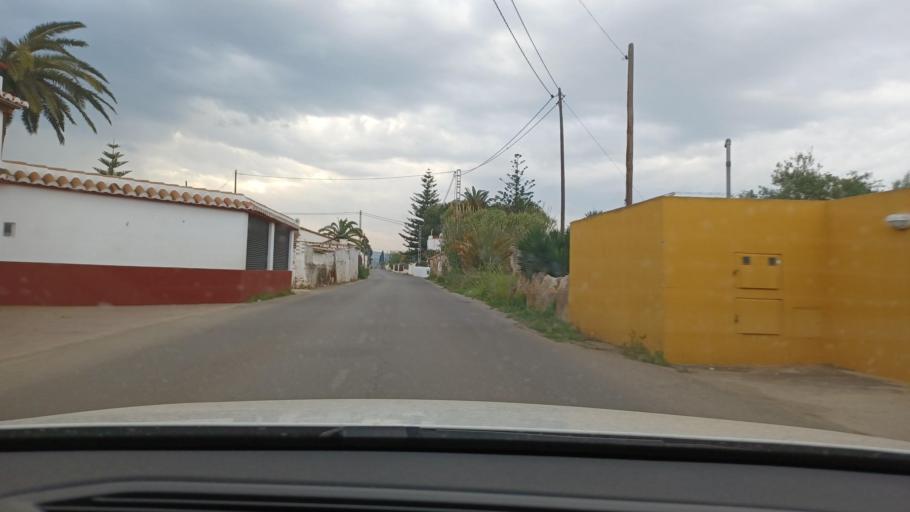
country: ES
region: Valencia
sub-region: Provincia de Castello
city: Benicarlo
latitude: 40.4018
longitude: 0.4124
